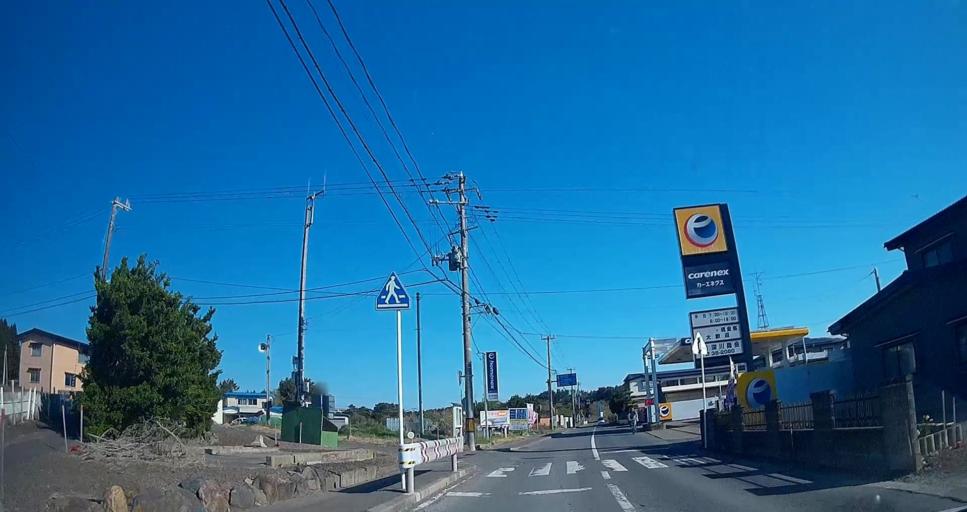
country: JP
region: Aomori
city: Hachinohe
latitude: 40.5108
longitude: 141.6073
